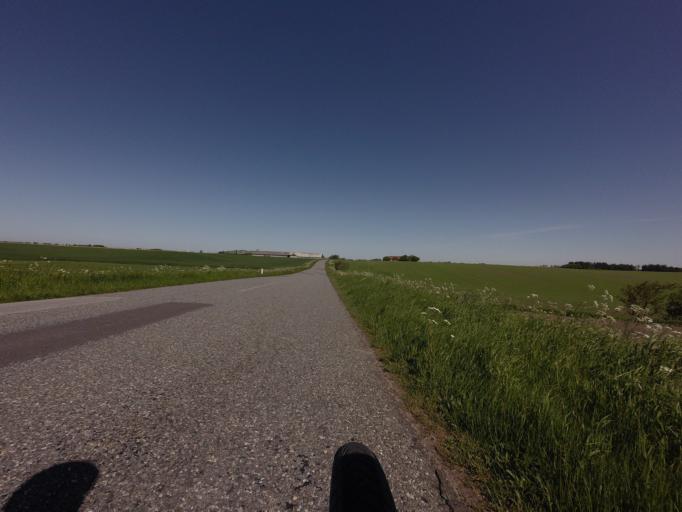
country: DK
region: North Denmark
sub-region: Hjorring Kommune
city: Hjorring
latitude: 57.4409
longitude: 9.8999
